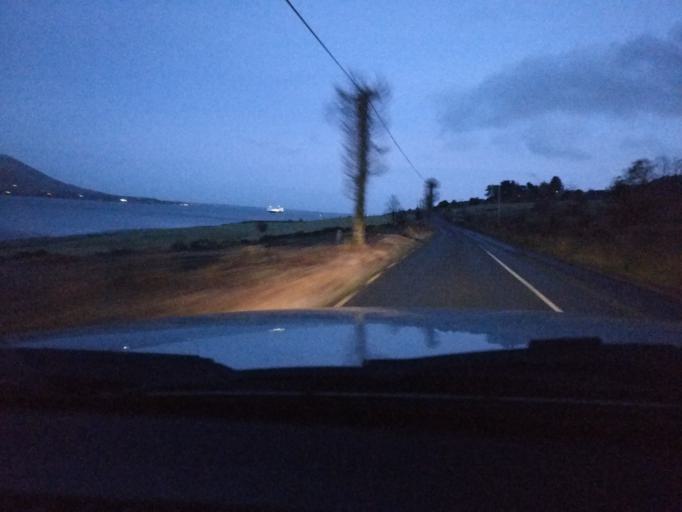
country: GB
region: Northern Ireland
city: Rostrevor
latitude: 54.0660
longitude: -6.2184
